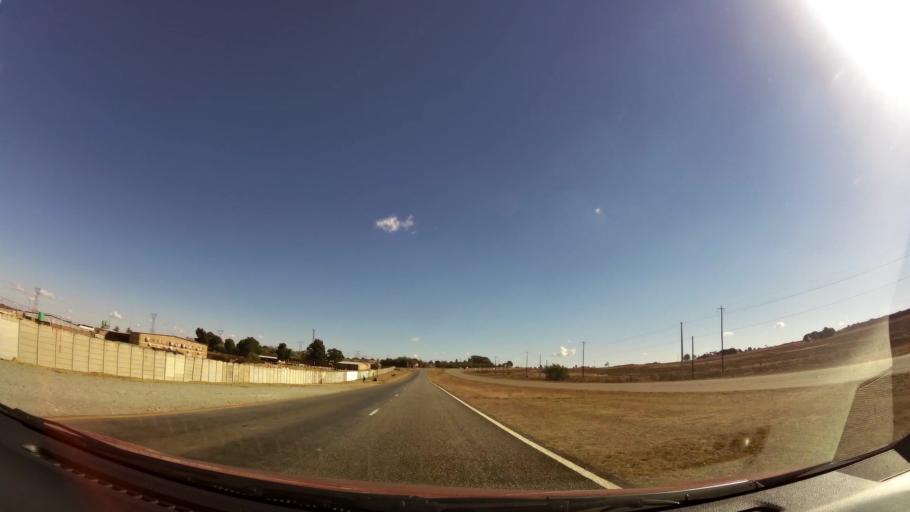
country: ZA
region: Gauteng
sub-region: West Rand District Municipality
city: Carletonville
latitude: -26.4166
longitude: 27.4465
